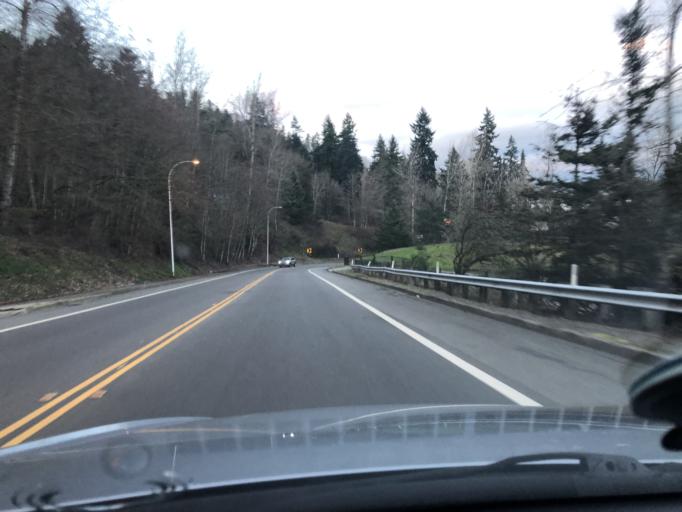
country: US
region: Washington
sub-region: King County
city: Lakeland North
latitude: 47.3213
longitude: -122.2561
